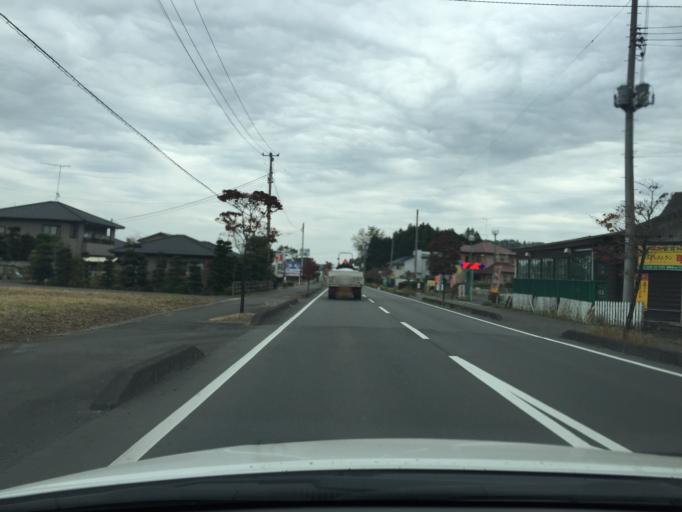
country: JP
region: Fukushima
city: Ishikawa
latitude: 37.1023
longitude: 140.2302
